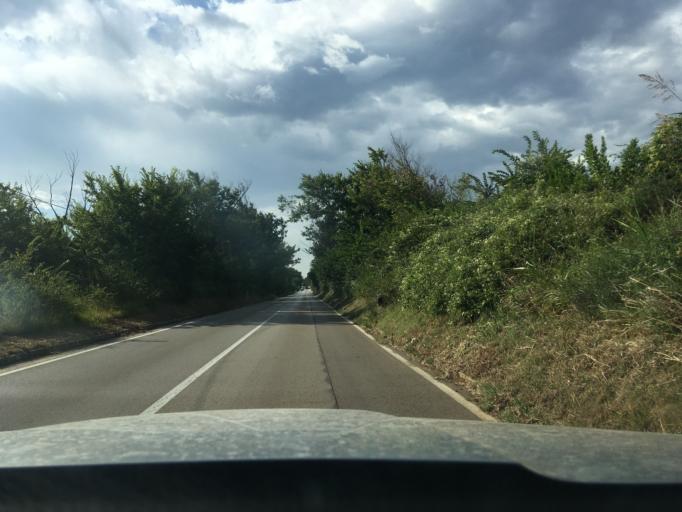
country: HR
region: Zadarska
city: Nin
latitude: 44.2341
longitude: 15.1884
